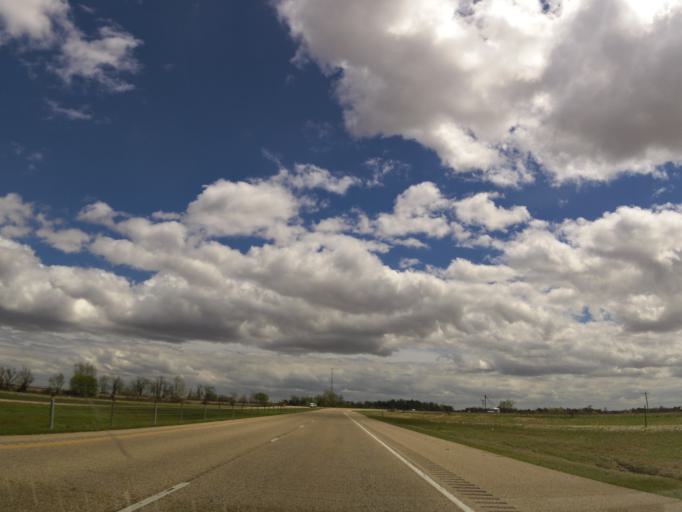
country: US
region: Arkansas
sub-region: Poinsett County
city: Marked Tree
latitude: 35.4722
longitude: -90.3323
